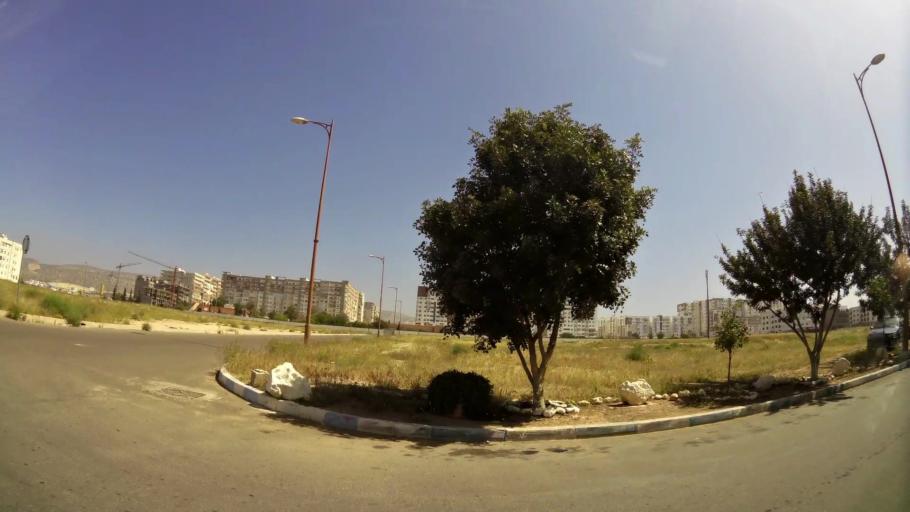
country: MA
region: Oued ed Dahab-Lagouira
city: Dakhla
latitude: 30.4326
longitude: -9.5651
